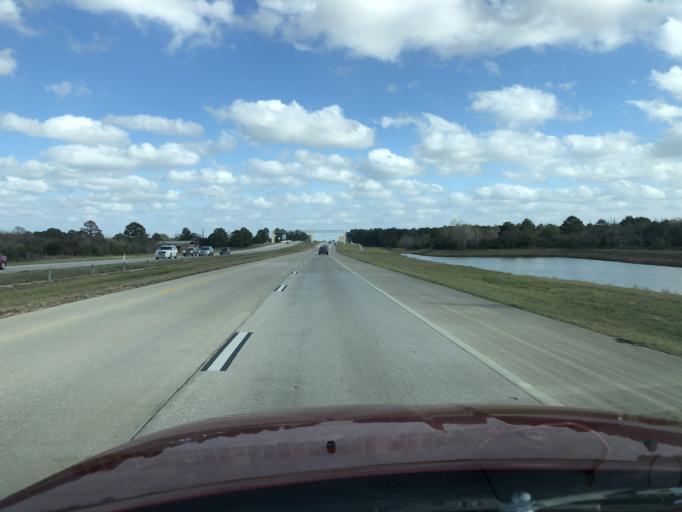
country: US
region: Texas
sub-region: Harris County
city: Tomball
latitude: 30.0520
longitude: -95.6436
